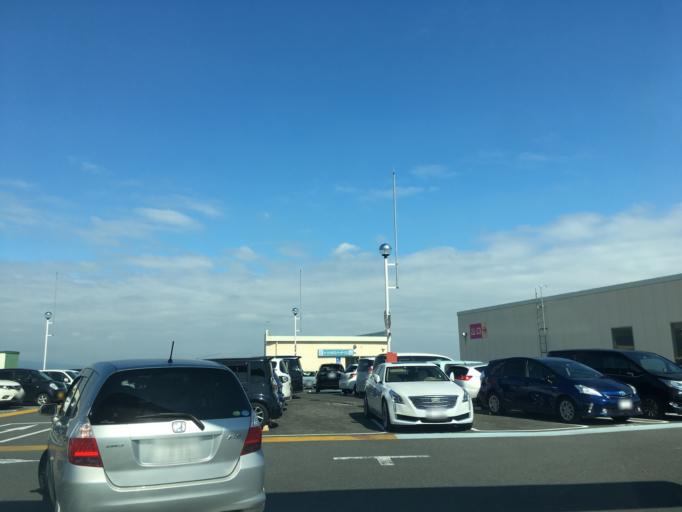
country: JP
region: Gunma
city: Kanekomachi
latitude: 36.3909
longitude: 139.0061
